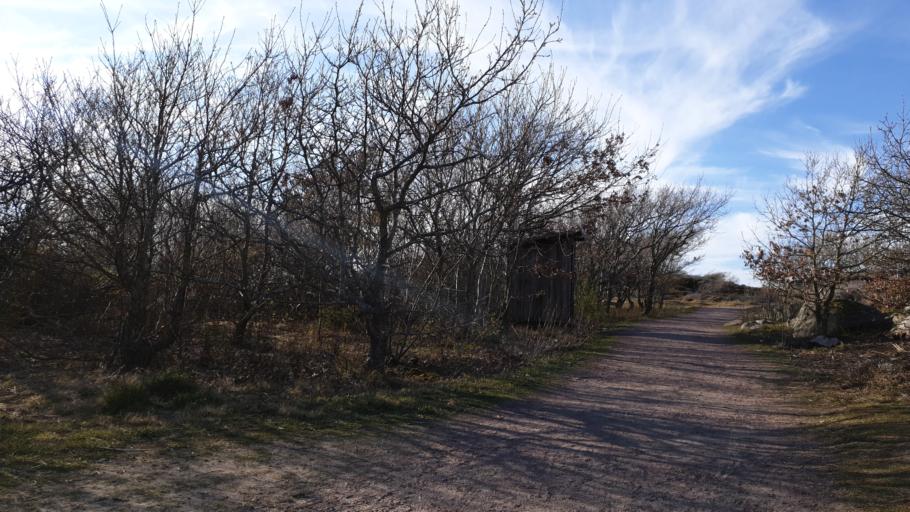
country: SE
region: Vaestra Goetaland
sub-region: Goteborg
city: Billdal
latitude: 57.5919
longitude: 11.9032
